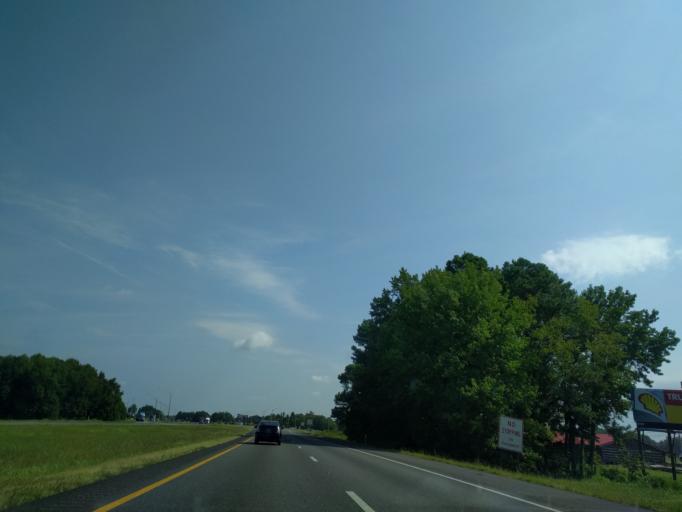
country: US
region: Tennessee
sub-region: Sumner County
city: Portland
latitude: 36.6060
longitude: -86.5831
